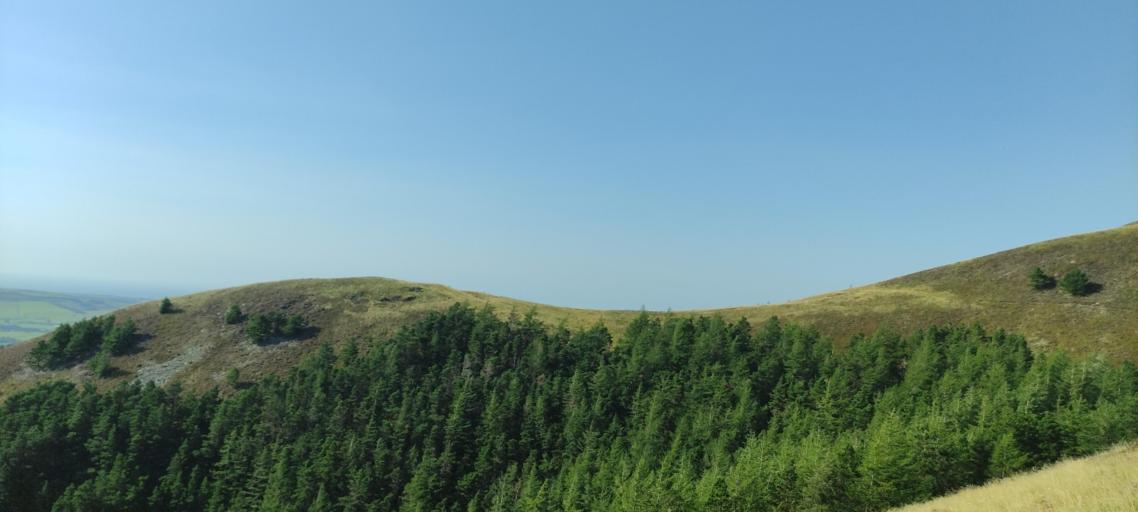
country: GB
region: England
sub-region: Cumbria
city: Cockermouth
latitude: 54.5654
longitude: -3.3846
